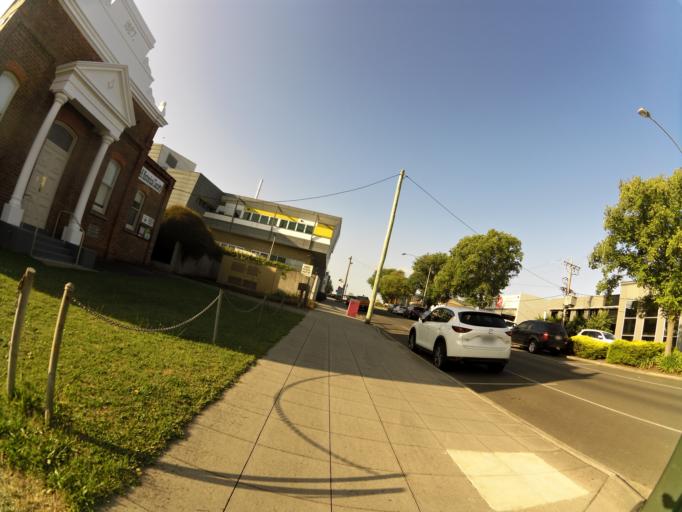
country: AU
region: Victoria
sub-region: Latrobe
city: Morwell
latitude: -38.2377
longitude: 146.3944
